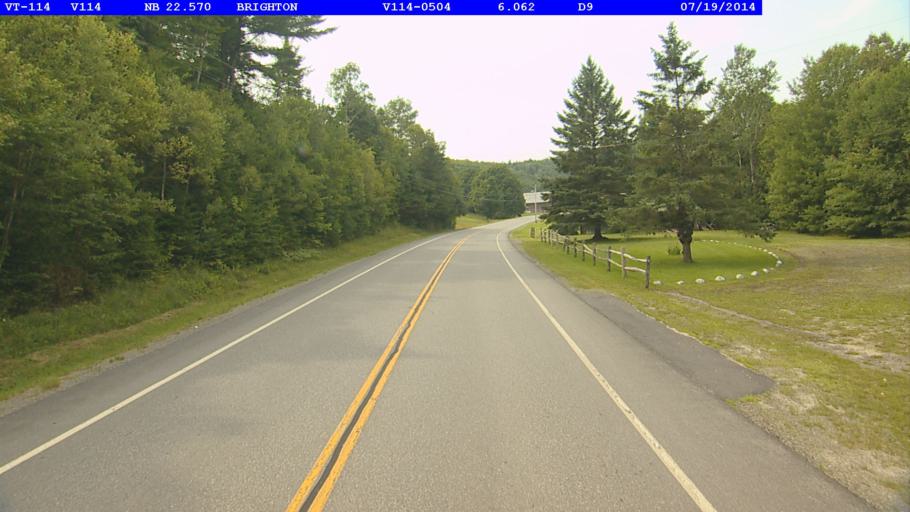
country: US
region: Vermont
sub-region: Caledonia County
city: Lyndonville
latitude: 44.8289
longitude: -71.9060
